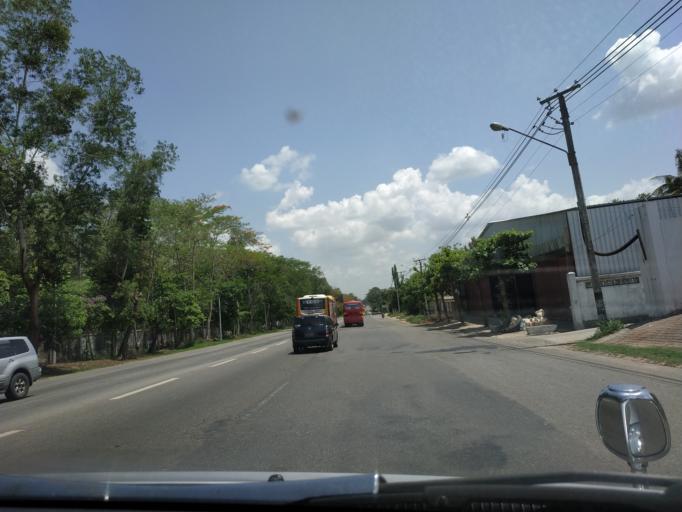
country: MM
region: Yangon
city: Yangon
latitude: 16.9945
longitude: 96.1309
